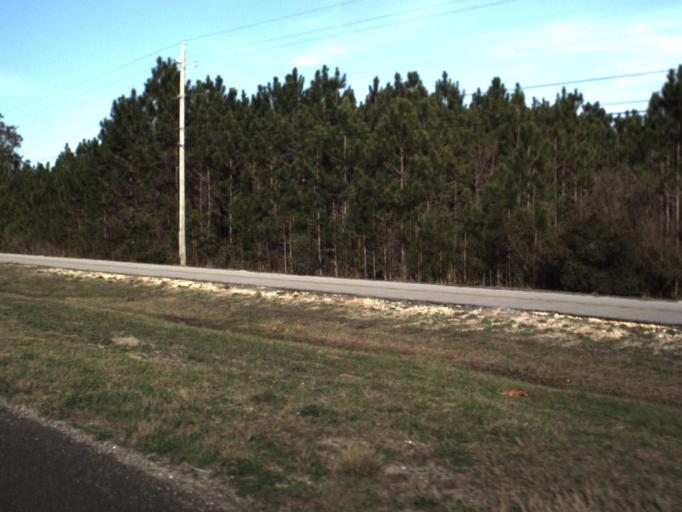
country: US
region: Florida
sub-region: Bay County
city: Laguna Beach
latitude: 30.2605
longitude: -85.8746
